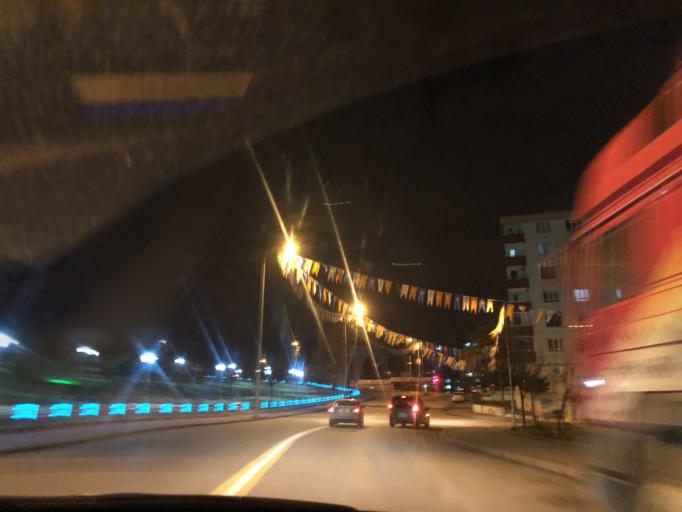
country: TR
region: Ankara
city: Batikent
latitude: 39.9685
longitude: 32.7803
